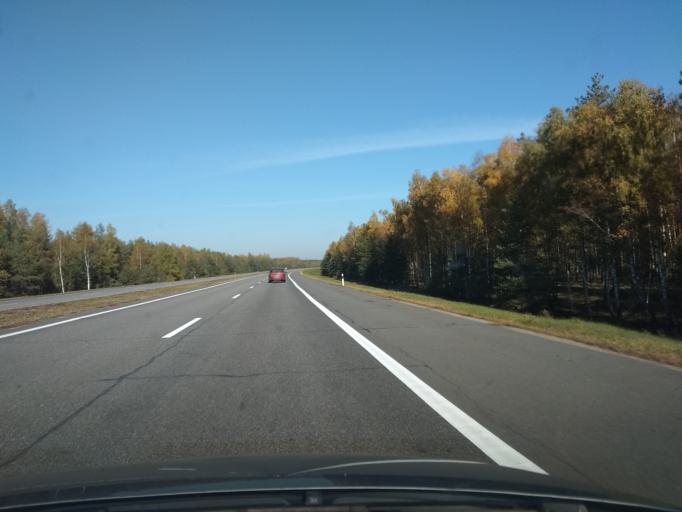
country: BY
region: Grodnenskaya
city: Zhyrovichy
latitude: 52.9190
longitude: 25.6863
